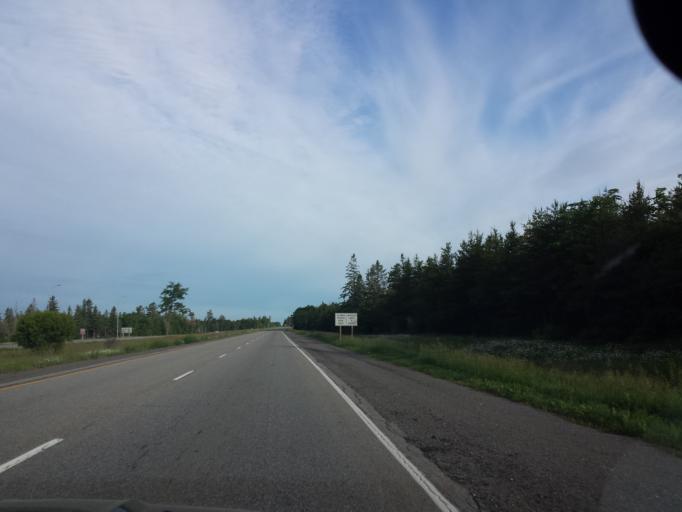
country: CA
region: Ontario
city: Carleton Place
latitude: 45.3338
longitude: -76.1670
